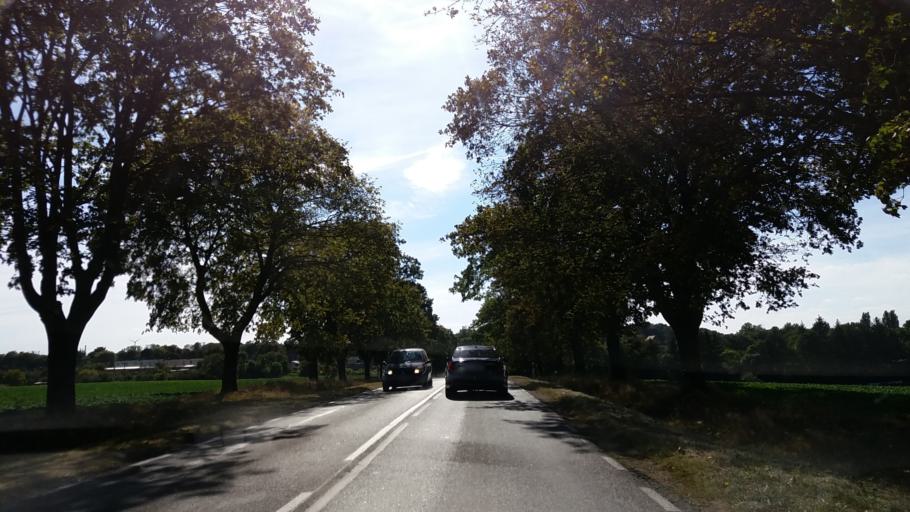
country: PL
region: Greater Poland Voivodeship
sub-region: Powiat miedzychodzki
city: Miedzychod
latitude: 52.5715
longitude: 15.8965
